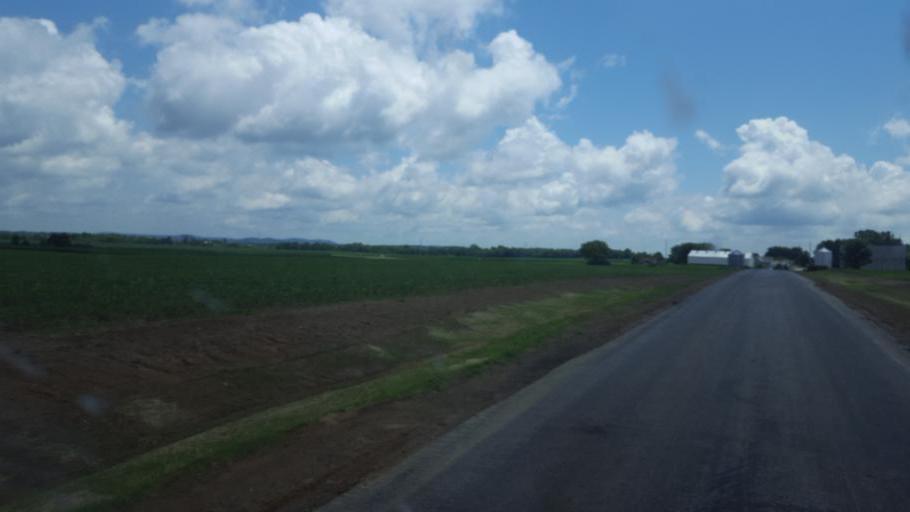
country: US
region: Ohio
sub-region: Highland County
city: Greenfield
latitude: 39.2650
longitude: -83.4482
